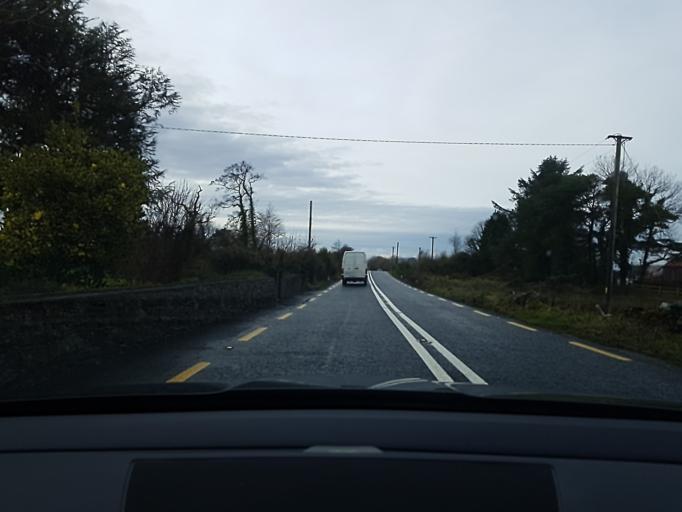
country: IE
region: Connaught
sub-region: Maigh Eo
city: Castlebar
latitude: 53.8324
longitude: -9.2976
